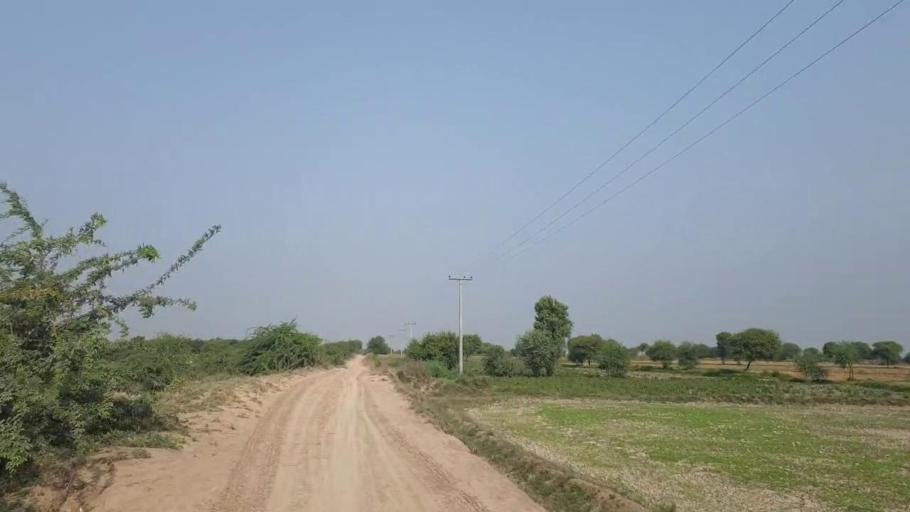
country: PK
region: Sindh
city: Badin
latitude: 24.6967
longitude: 68.7783
